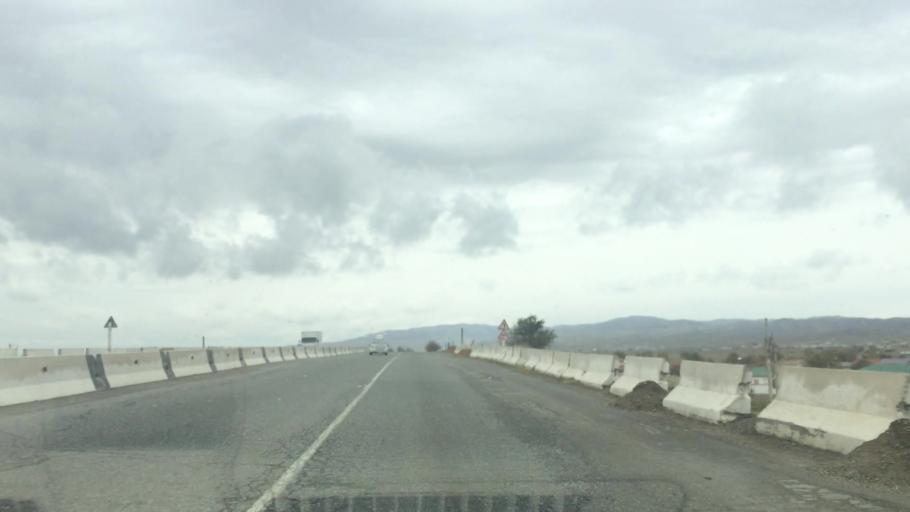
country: UZ
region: Samarqand
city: Bulung'ur
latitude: 39.8371
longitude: 67.4382
